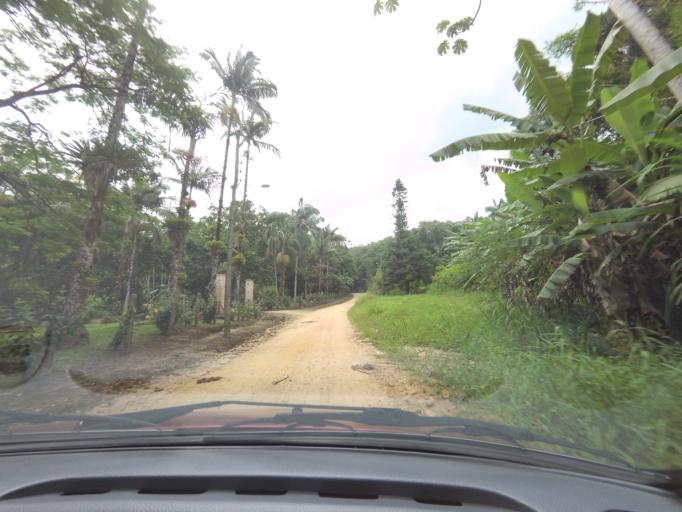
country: BR
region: Santa Catarina
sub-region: Brusque
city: Brusque
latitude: -27.0536
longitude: -48.9970
